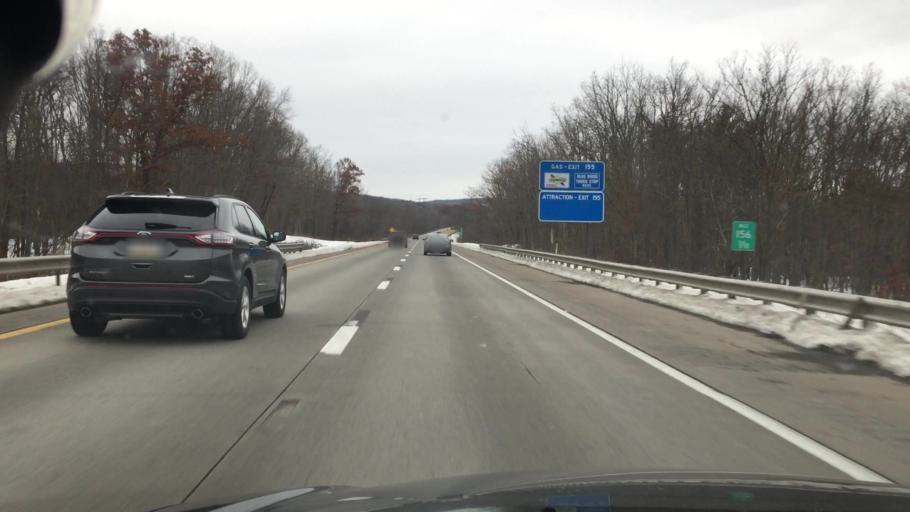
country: US
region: Pennsylvania
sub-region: Luzerne County
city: Mountain Top
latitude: 41.1111
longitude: -75.9615
